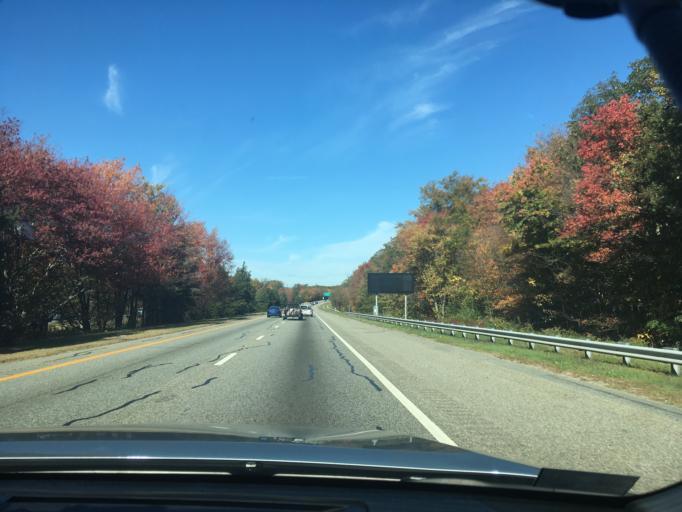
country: US
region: Rhode Island
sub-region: Providence County
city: Johnston
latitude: 41.7926
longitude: -71.5076
